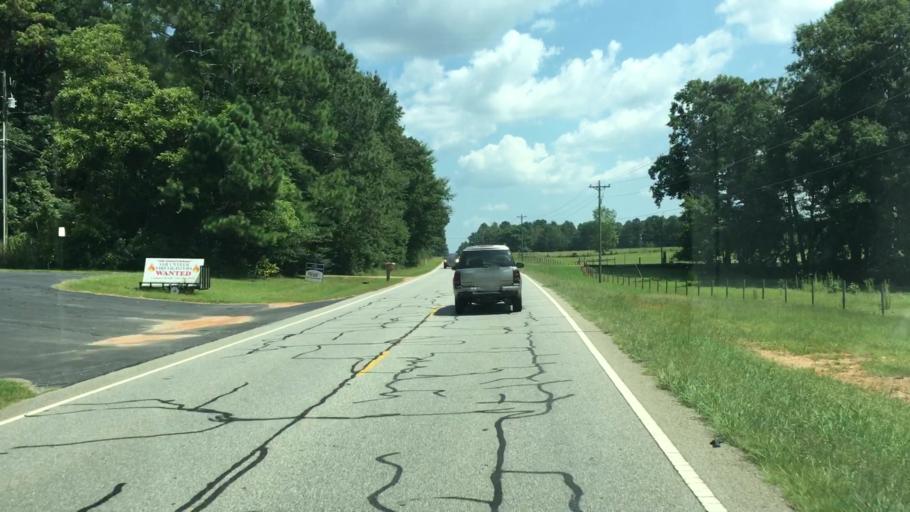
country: US
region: Georgia
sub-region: Barrow County
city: Statham
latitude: 33.9122
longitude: -83.5976
